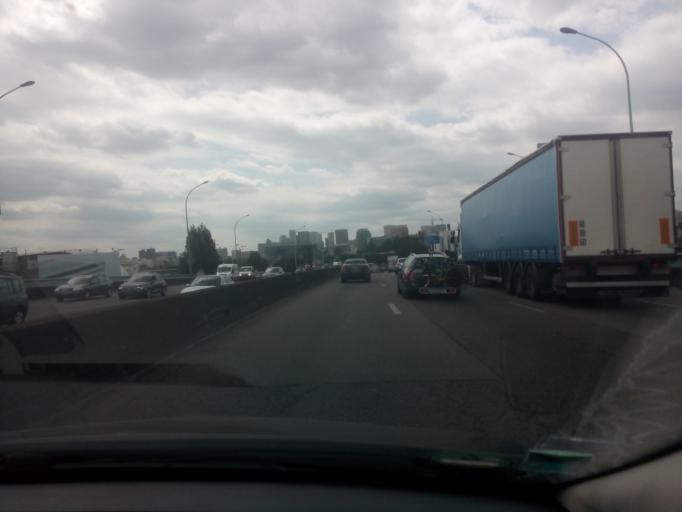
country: FR
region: Ile-de-France
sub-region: Departement du Val-de-Marne
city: Ivry-sur-Seine
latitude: 48.8280
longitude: 2.3953
